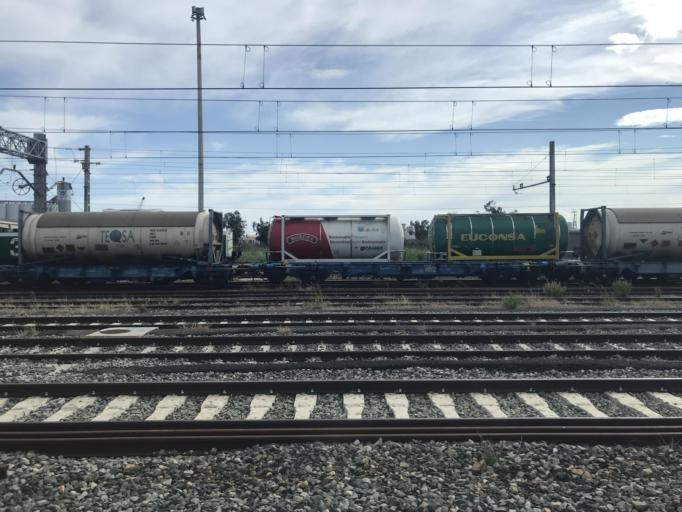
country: ES
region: Catalonia
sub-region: Provincia de Tarragona
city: Tarragona
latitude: 41.1109
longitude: 1.2261
